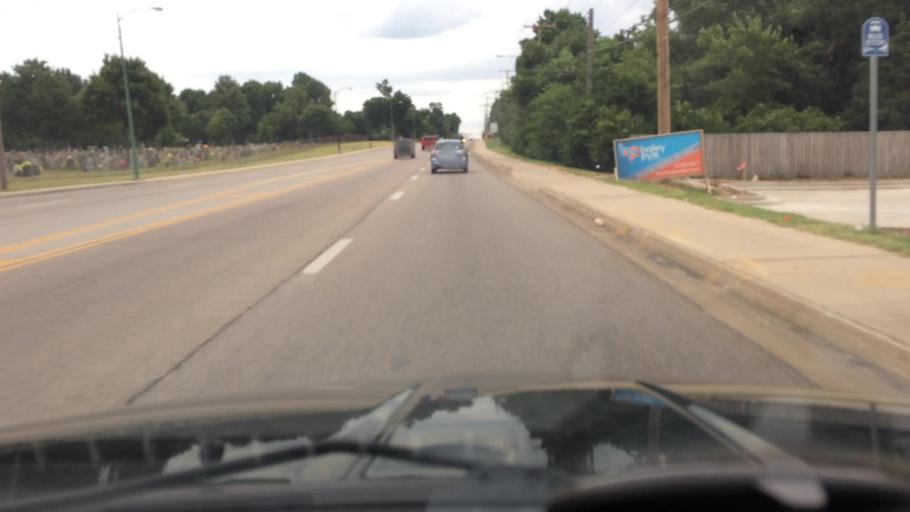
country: US
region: Missouri
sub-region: Greene County
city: Springfield
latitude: 37.1675
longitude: -93.2625
